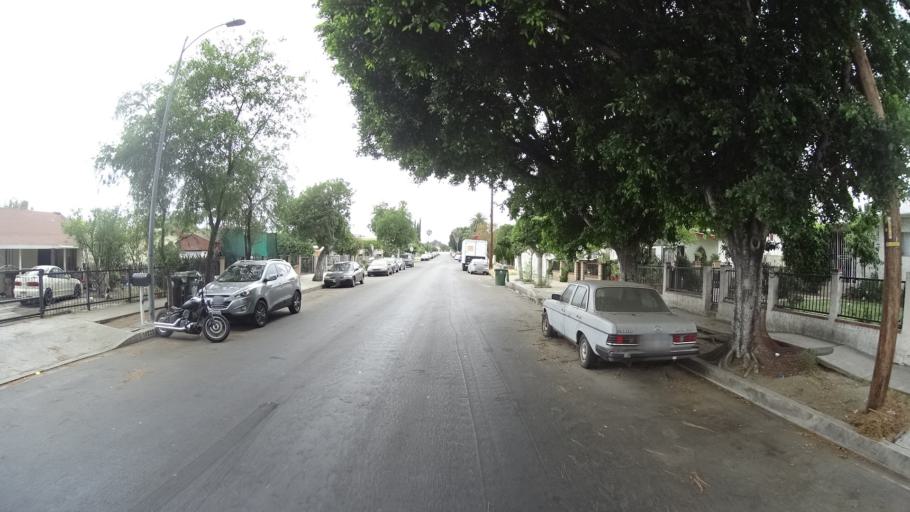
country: US
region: California
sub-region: Los Angeles County
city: San Fernando
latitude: 34.2560
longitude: -118.4381
